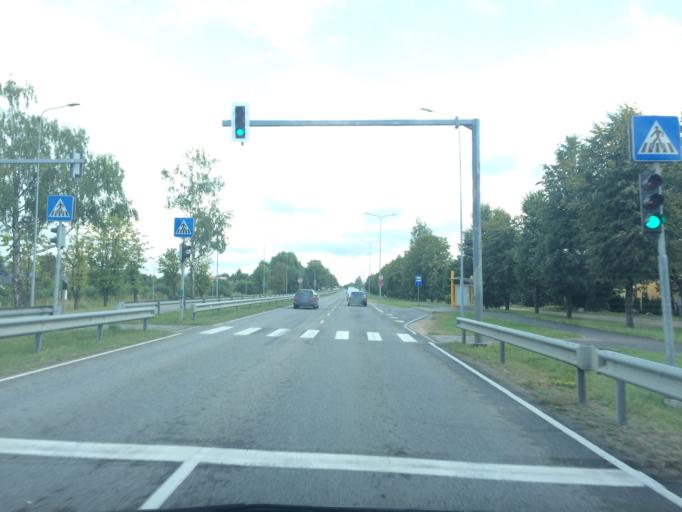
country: LV
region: Ogre
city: Ogre
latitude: 56.8027
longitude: 24.6138
